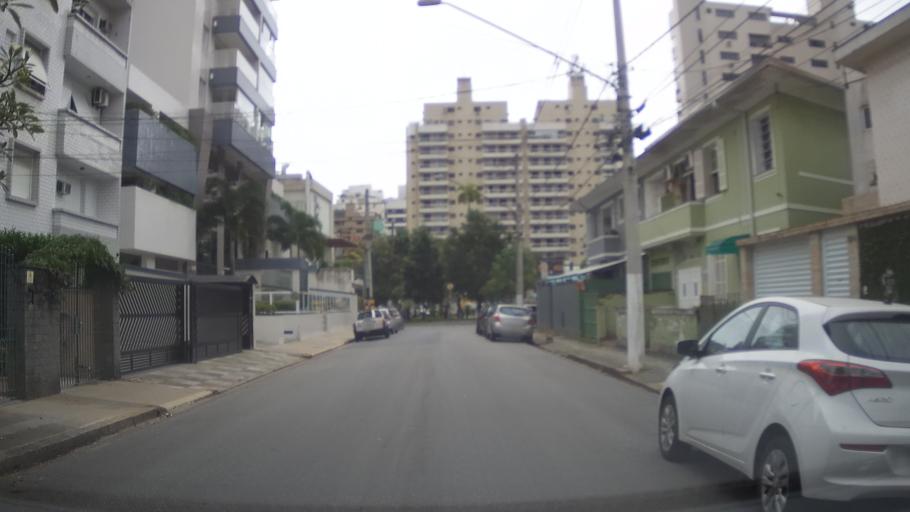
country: BR
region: Sao Paulo
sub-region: Santos
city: Santos
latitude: -23.9705
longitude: -46.3195
